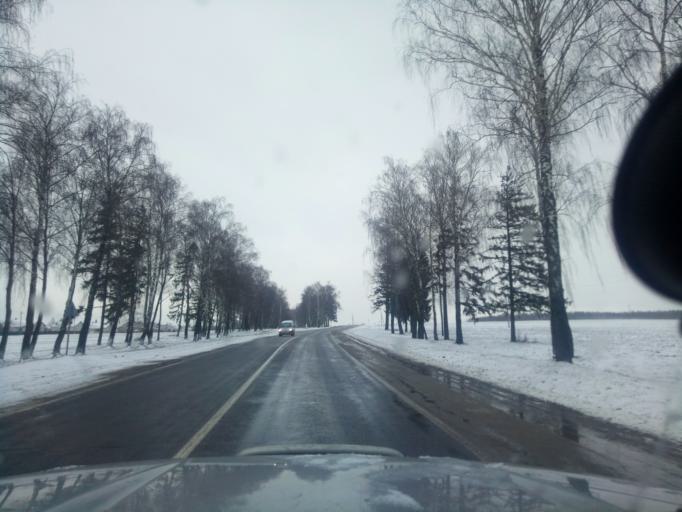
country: BY
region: Minsk
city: Kapyl'
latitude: 53.1079
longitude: 27.0571
